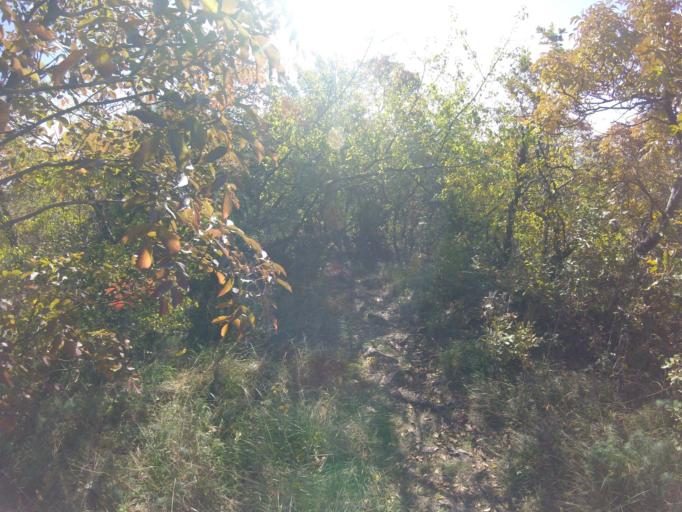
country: HU
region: Pest
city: Csobanka
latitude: 47.6293
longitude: 18.9725
